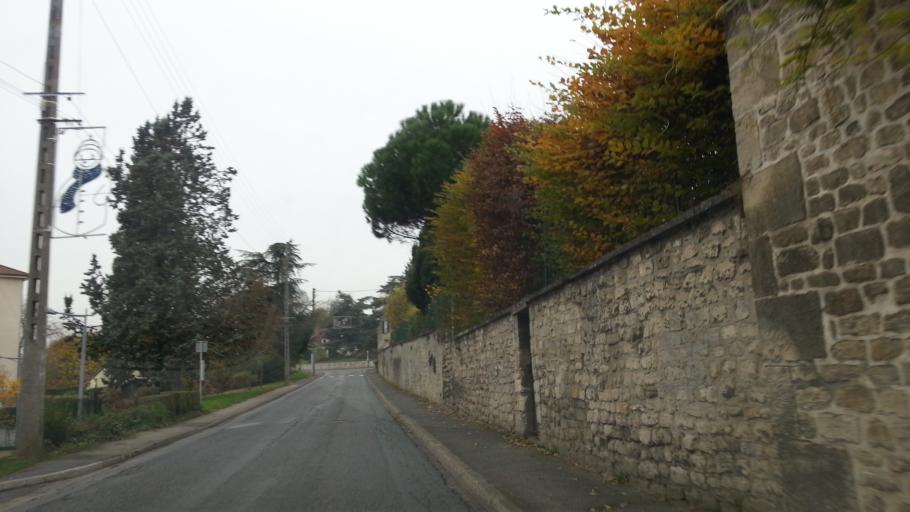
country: FR
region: Picardie
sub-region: Departement de l'Oise
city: Villers-sous-Saint-Leu
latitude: 49.2160
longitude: 2.4127
